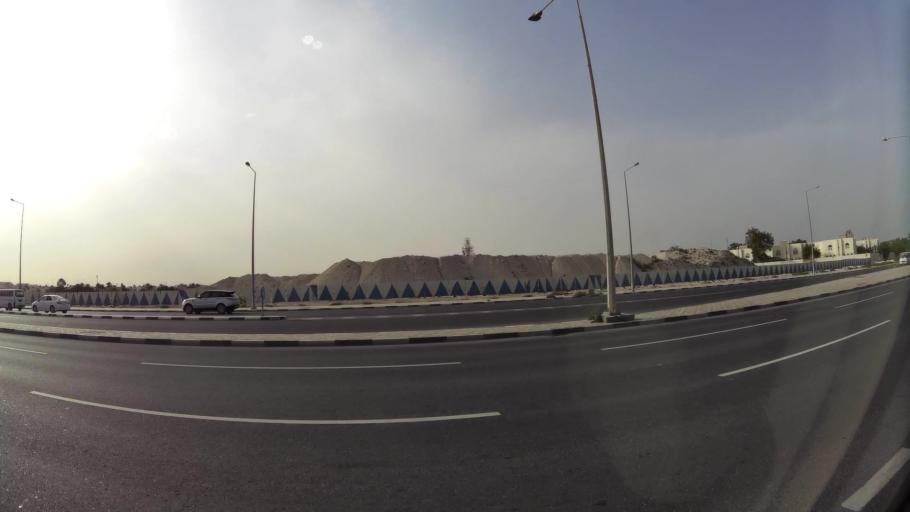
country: QA
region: Baladiyat ad Dawhah
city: Doha
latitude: 25.3215
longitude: 51.5149
